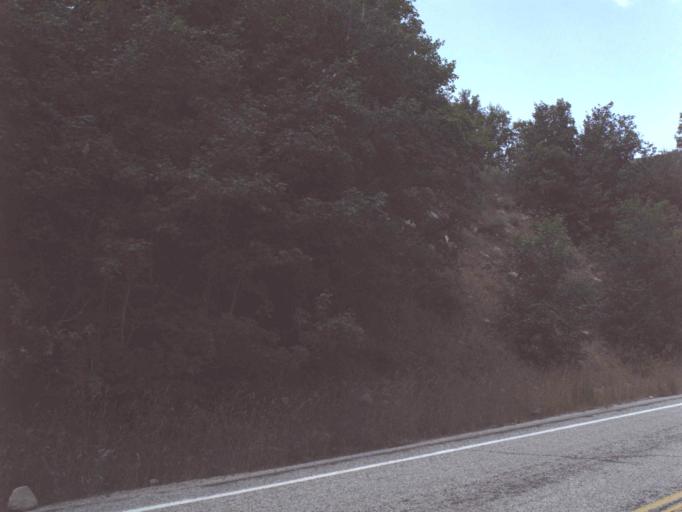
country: US
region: Utah
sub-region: Weber County
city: Wolf Creek
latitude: 41.3216
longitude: -111.6158
